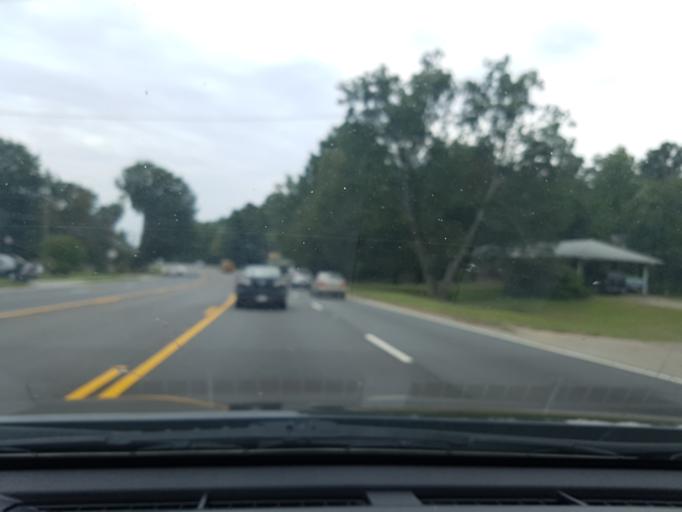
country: US
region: Georgia
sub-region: Gwinnett County
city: Duluth
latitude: 33.9921
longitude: -84.1524
